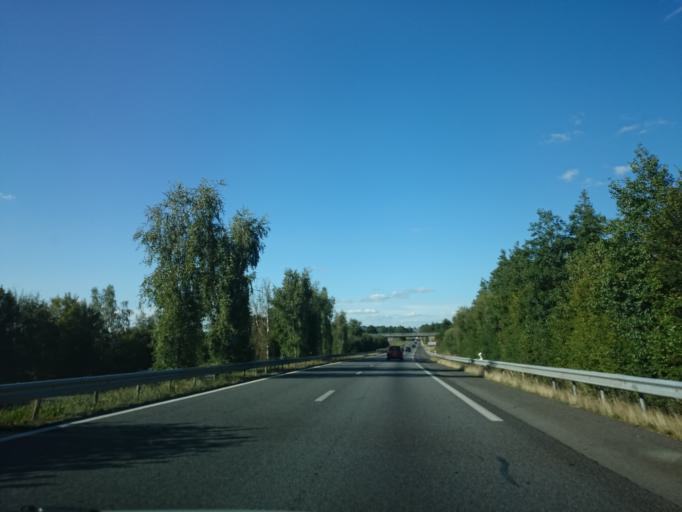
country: FR
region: Brittany
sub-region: Departement d'Ille-et-Vilaine
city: Bain-de-Bretagne
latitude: 47.8058
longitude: -1.6902
